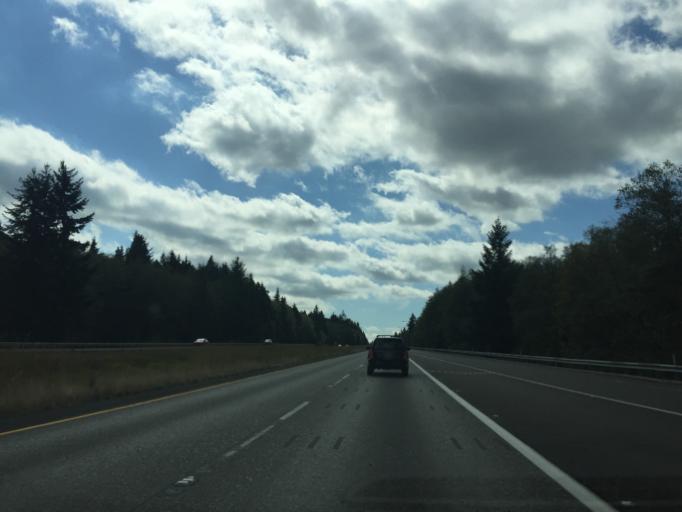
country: US
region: Washington
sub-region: Skagit County
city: Burlington
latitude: 48.5828
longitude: -122.3461
